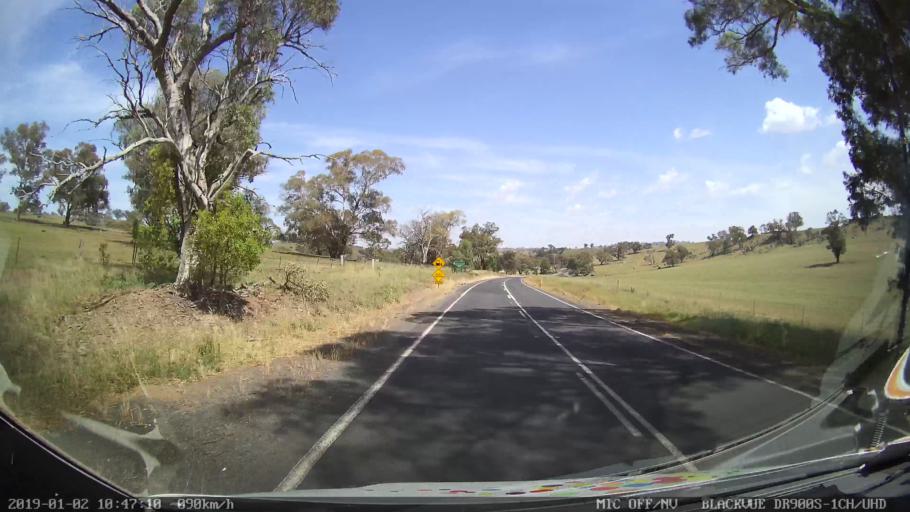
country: AU
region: New South Wales
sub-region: Cootamundra
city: Cootamundra
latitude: -34.7478
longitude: 148.2764
